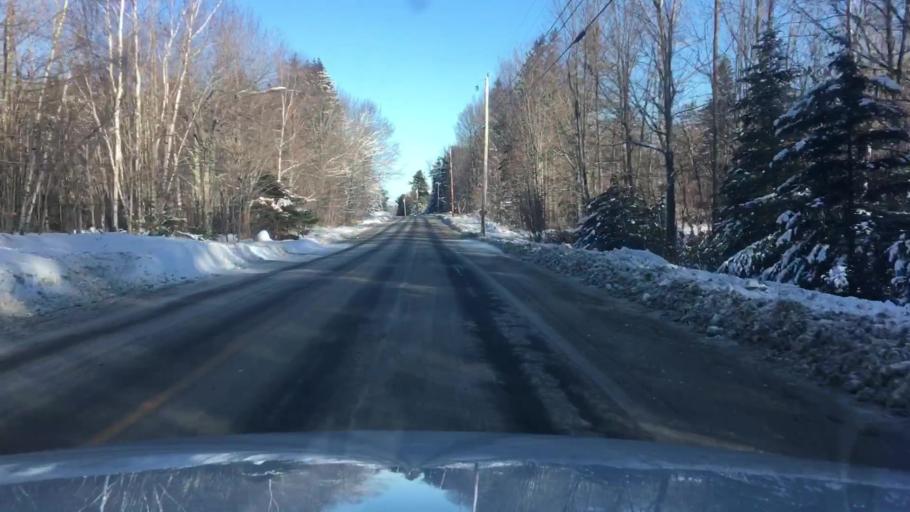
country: US
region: Maine
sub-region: Kennebec County
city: Mount Vernon
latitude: 44.4536
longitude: -69.9706
